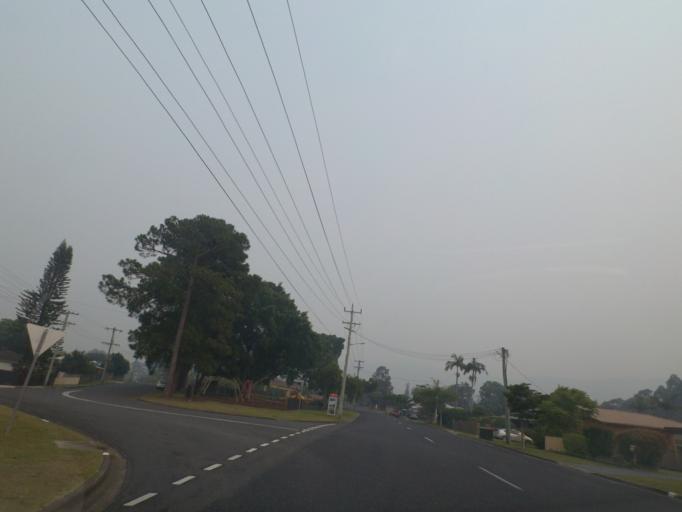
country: AU
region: New South Wales
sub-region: Coffs Harbour
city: Coffs Harbour
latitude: -30.2872
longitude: 153.1078
